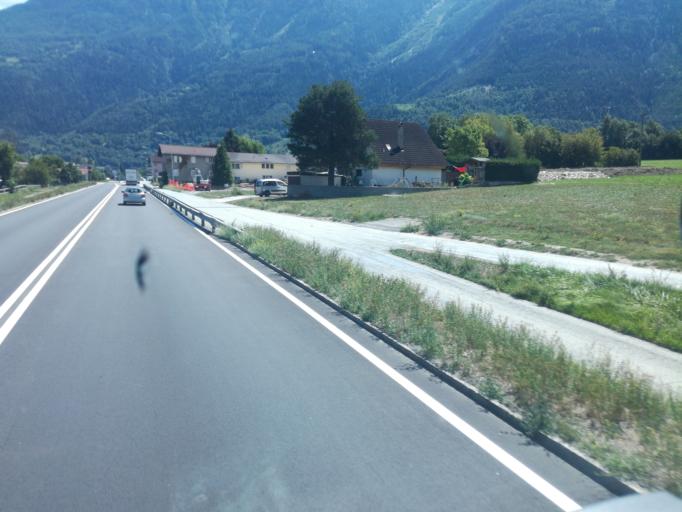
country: CH
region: Valais
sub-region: Leuk District
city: Leuk
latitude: 46.3064
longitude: 7.6536
